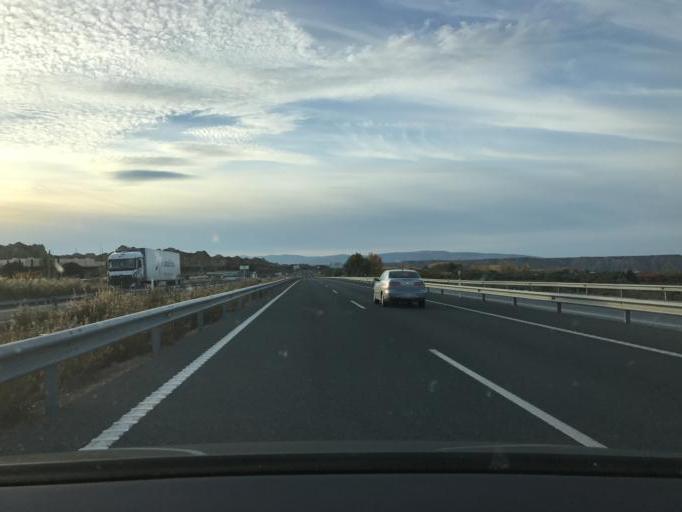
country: ES
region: Andalusia
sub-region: Provincia de Granada
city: Guadix
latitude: 37.3201
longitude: -3.1538
